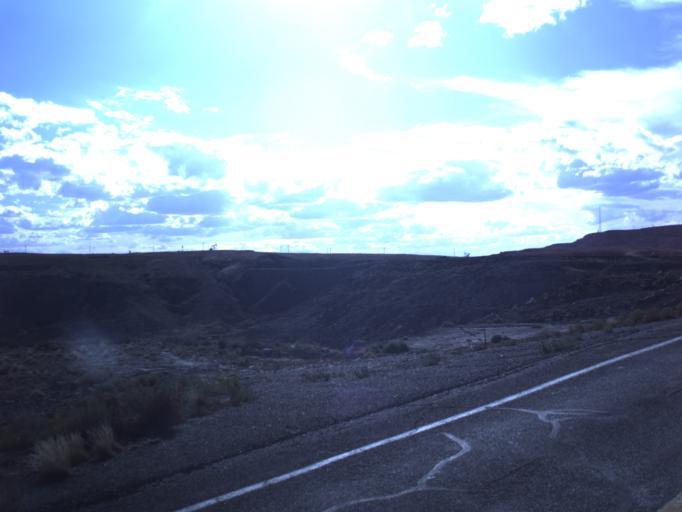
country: US
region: Utah
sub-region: San Juan County
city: Blanding
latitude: 37.3220
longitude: -109.3188
